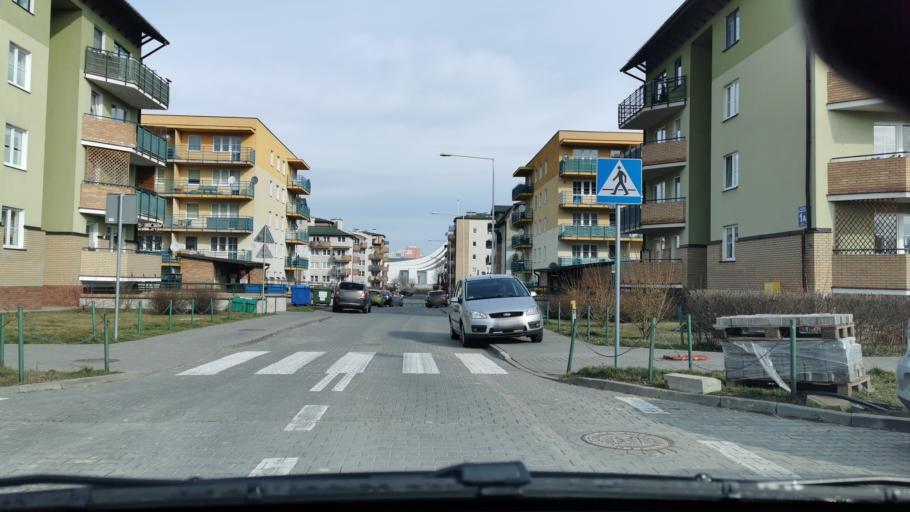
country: PL
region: Lublin Voivodeship
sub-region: Powiat lubelski
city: Lublin
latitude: 51.1990
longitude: 22.5458
